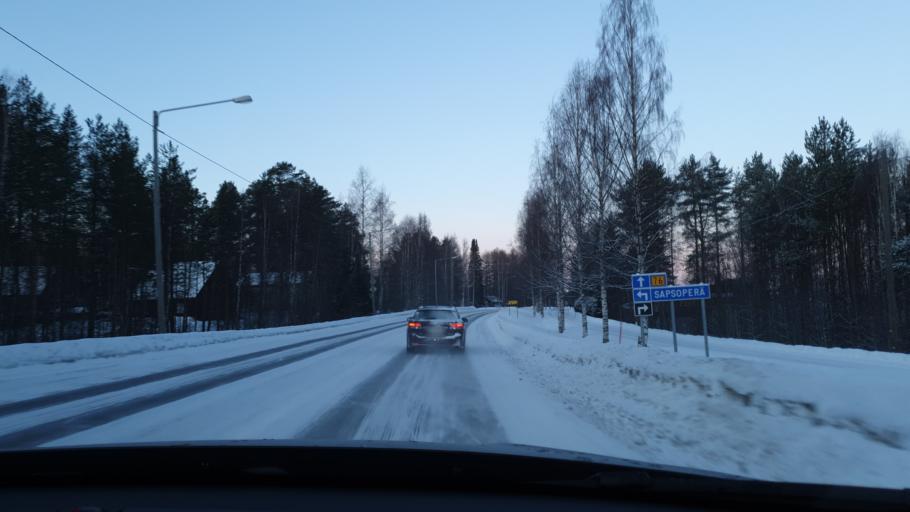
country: FI
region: Kainuu
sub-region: Kajaani
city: Sotkamo
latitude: 64.1232
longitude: 28.4296
